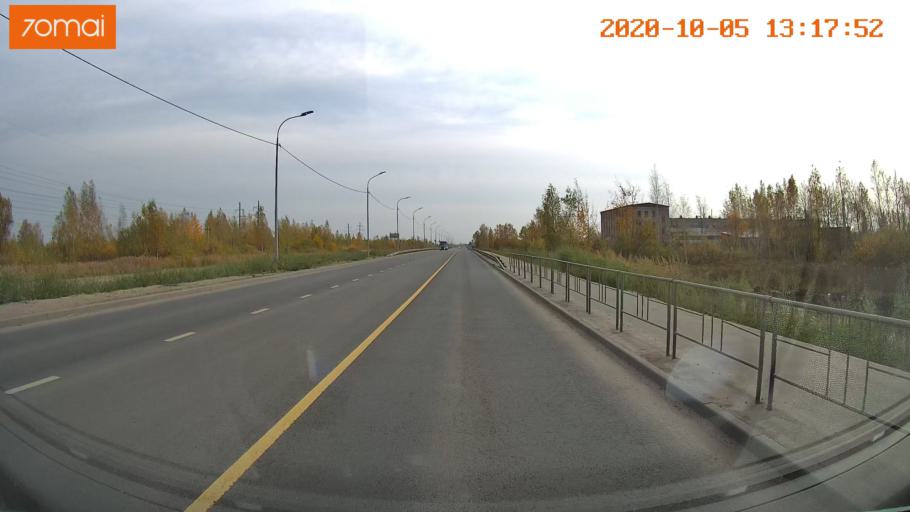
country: RU
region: Ivanovo
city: Novo-Talitsy
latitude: 56.9825
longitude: 40.9141
